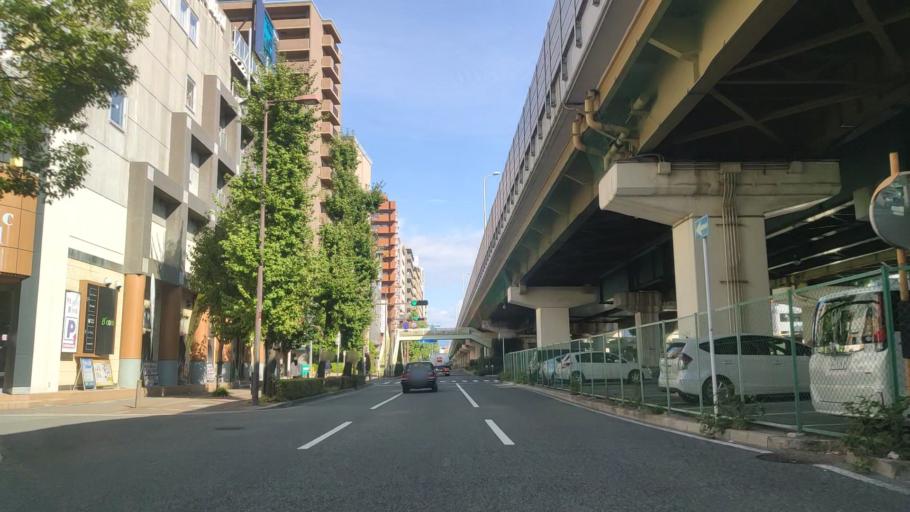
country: JP
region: Osaka
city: Suita
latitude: 34.7426
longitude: 135.4982
